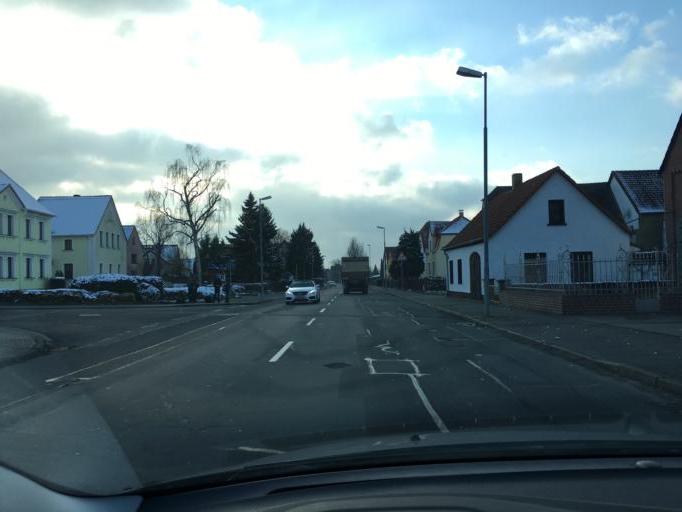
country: DE
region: Saxony
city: Brandis
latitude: 51.3568
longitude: 12.5838
